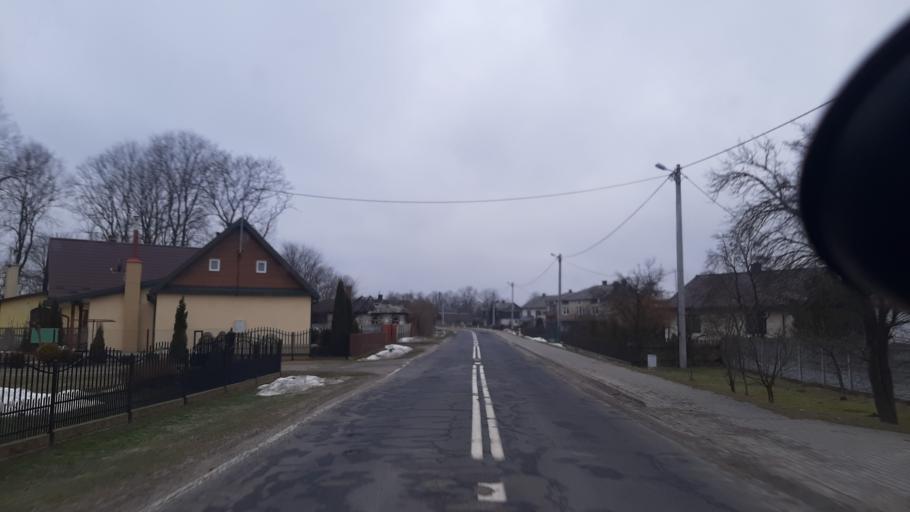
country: PL
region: Lublin Voivodeship
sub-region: Powiat wlodawski
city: Hansk
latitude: 51.5624
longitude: 23.3648
